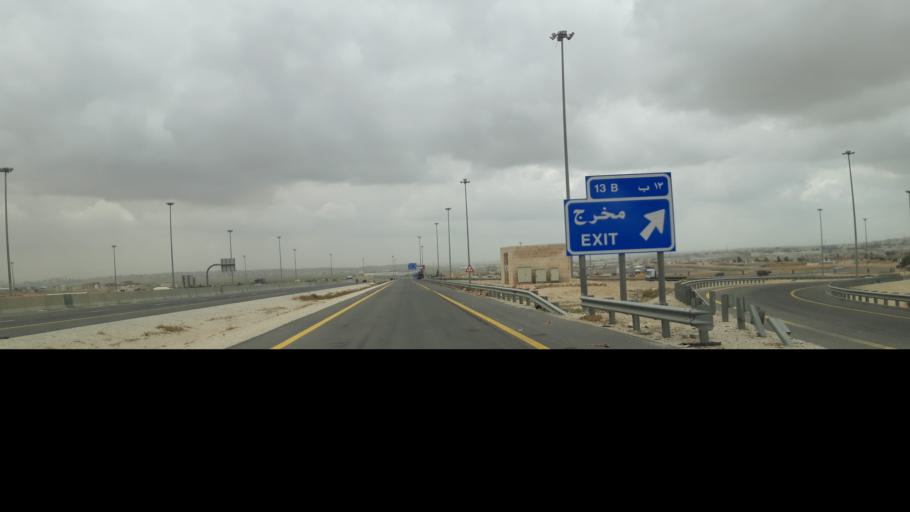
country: JO
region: Amman
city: Sahab
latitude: 31.8490
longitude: 36.0423
